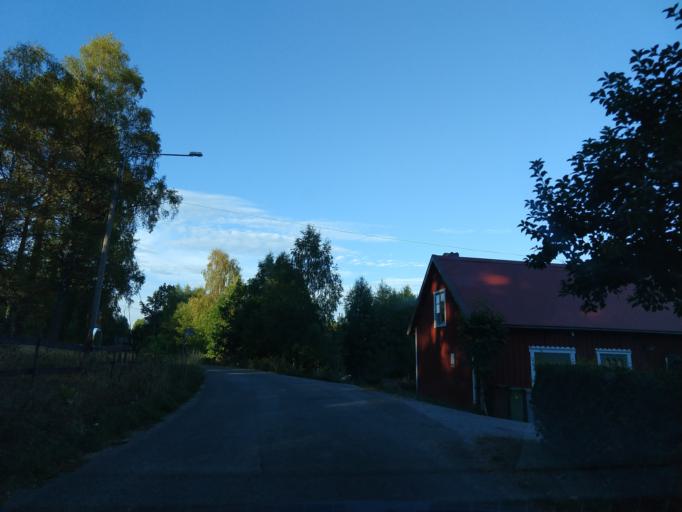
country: SE
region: Blekinge
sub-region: Ronneby Kommun
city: Brakne-Hoby
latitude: 56.2596
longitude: 15.1349
